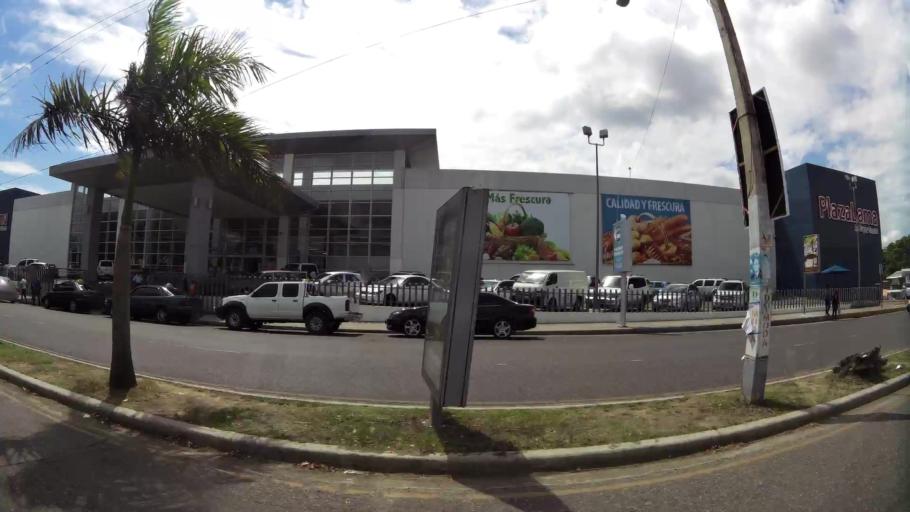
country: DO
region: Santiago
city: Santiago de los Caballeros
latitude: 19.4563
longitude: -70.7013
